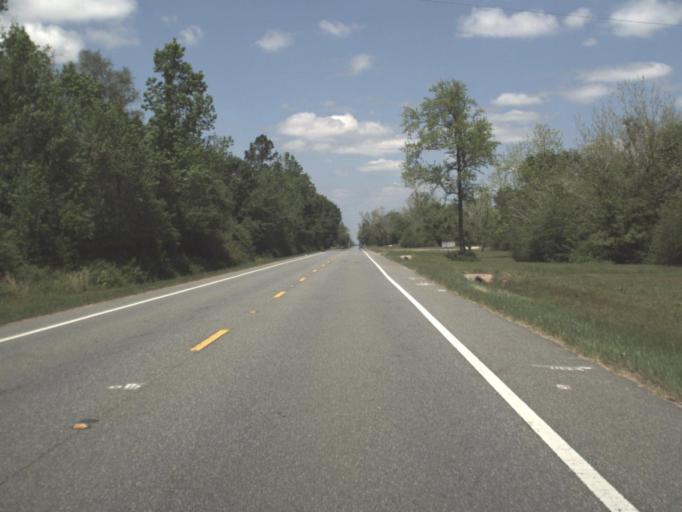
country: US
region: Florida
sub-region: Santa Rosa County
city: Point Baker
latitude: 30.7504
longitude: -87.0425
